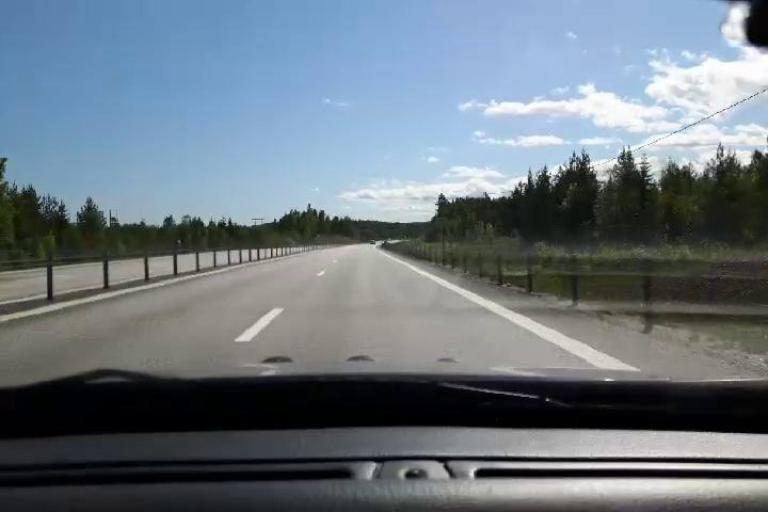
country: SE
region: Gaevleborg
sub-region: Hudiksvalls Kommun
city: Iggesund
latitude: 61.6730
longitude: 17.0322
